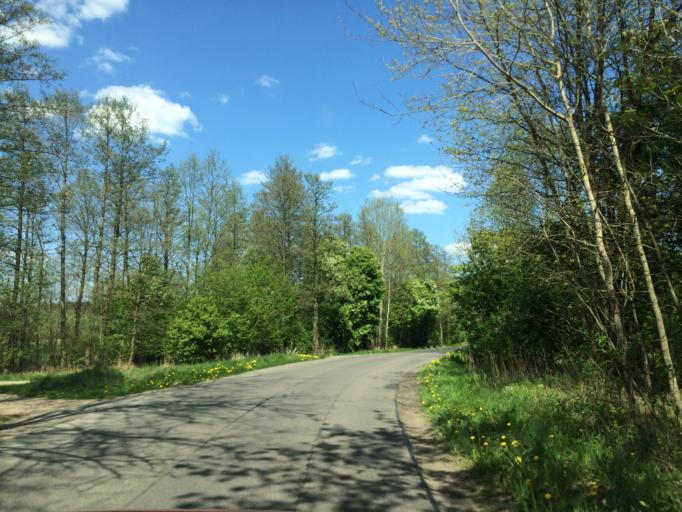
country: PL
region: Warmian-Masurian Voivodeship
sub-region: Powiat ilawski
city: Lubawa
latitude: 53.3956
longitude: 19.7385
